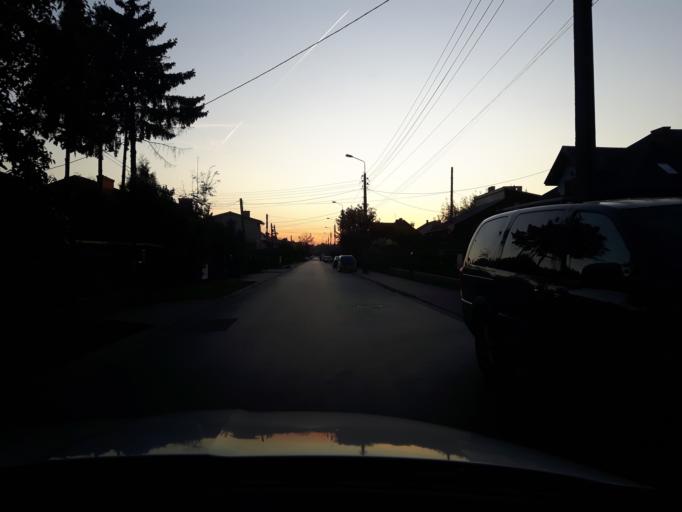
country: PL
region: Masovian Voivodeship
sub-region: Powiat wolominski
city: Kobylka
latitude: 52.3378
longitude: 21.1930
